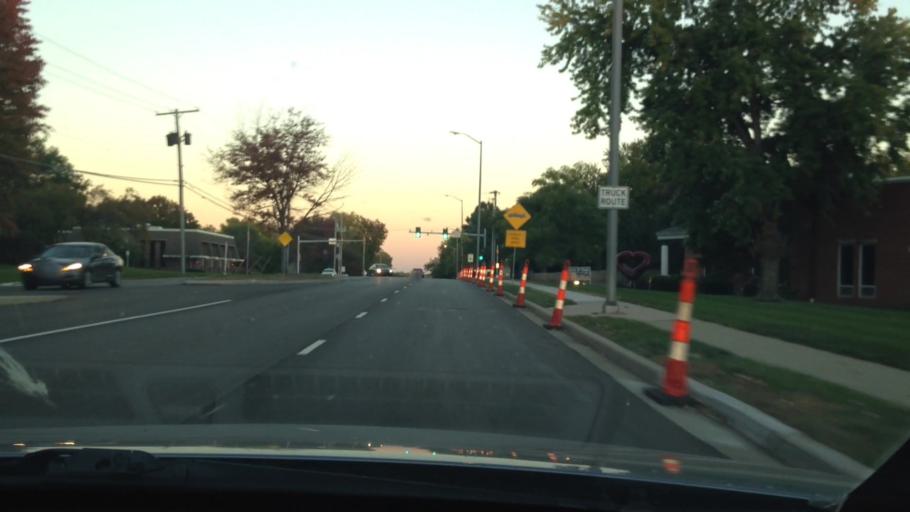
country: US
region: Kansas
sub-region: Johnson County
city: Overland Park
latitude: 38.9566
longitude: -94.6970
